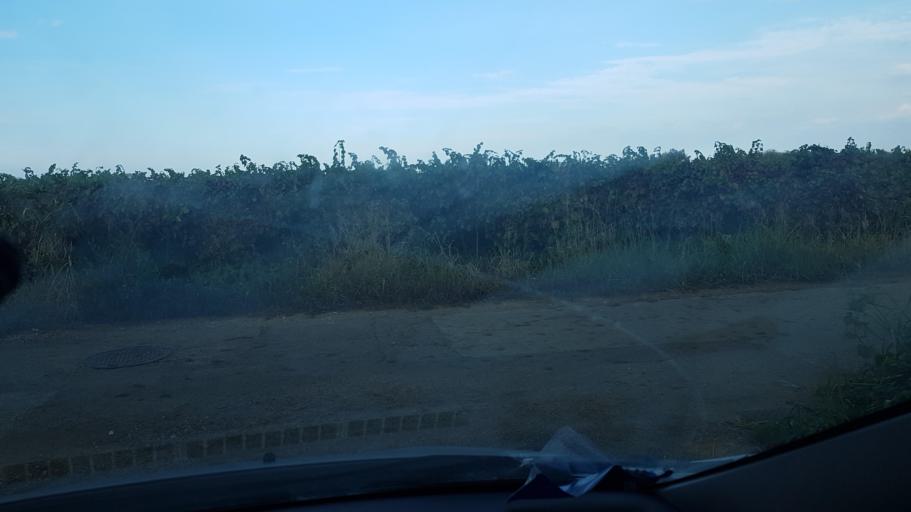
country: IT
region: Apulia
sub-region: Provincia di Brindisi
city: Cellino San Marco
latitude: 40.4697
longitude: 17.9744
